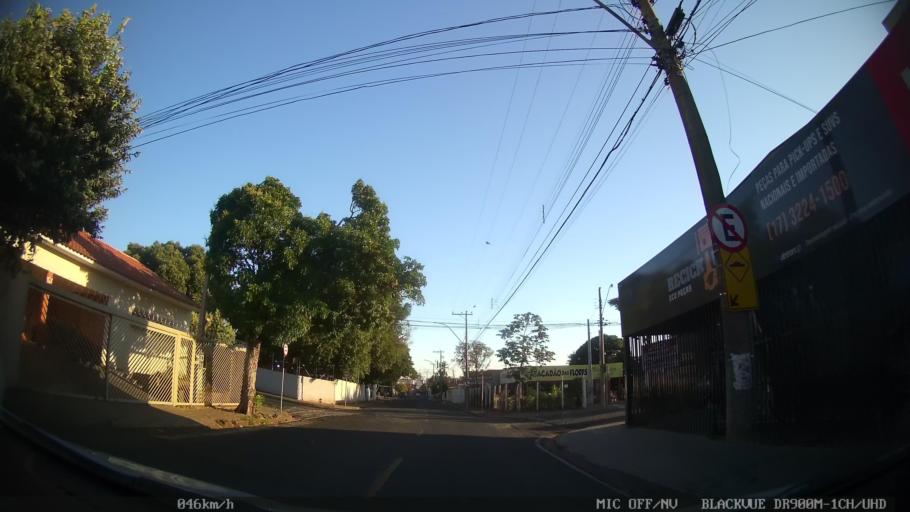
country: BR
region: Sao Paulo
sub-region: Sao Jose Do Rio Preto
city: Sao Jose do Rio Preto
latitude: -20.8005
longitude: -49.3718
